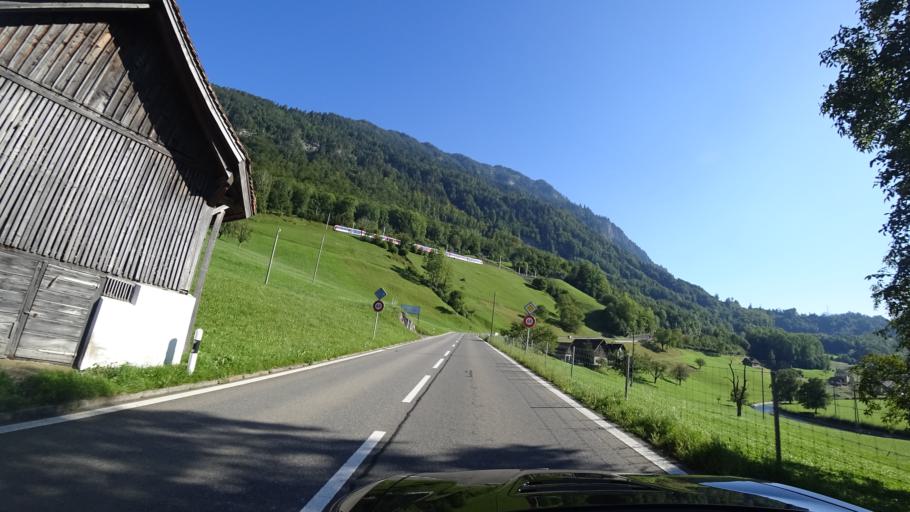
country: CH
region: Obwalden
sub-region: Obwalden
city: Giswil
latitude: 46.8299
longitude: 8.1848
